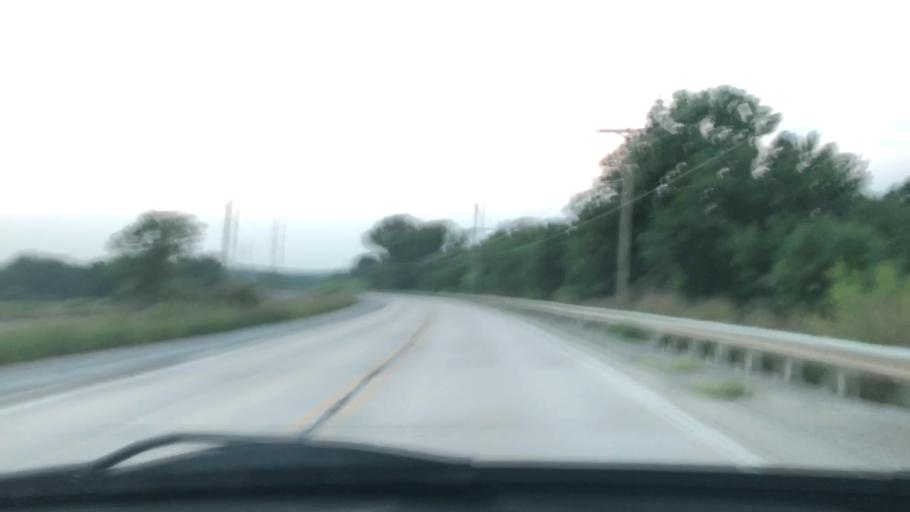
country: US
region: Iowa
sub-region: Johnson County
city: North Liberty
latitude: 41.8095
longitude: -91.6550
